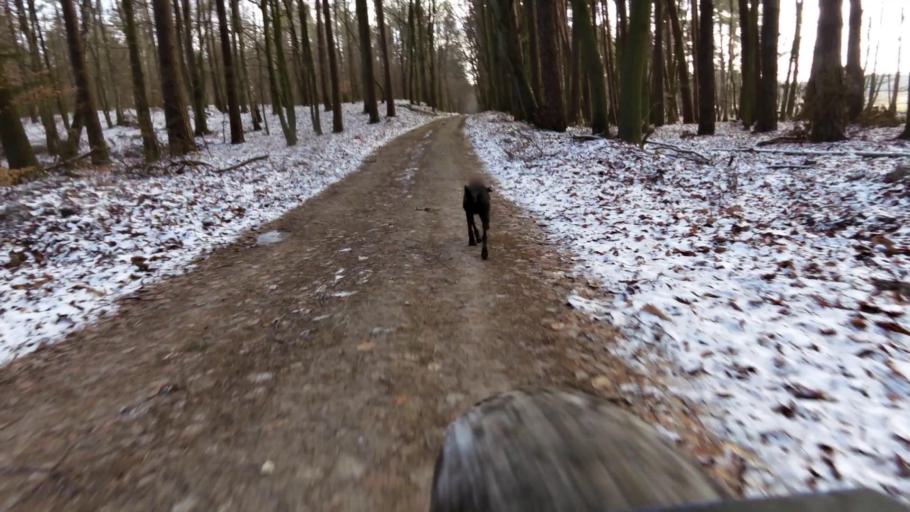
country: PL
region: West Pomeranian Voivodeship
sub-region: Powiat walecki
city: Walcz
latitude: 53.2813
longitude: 16.3045
